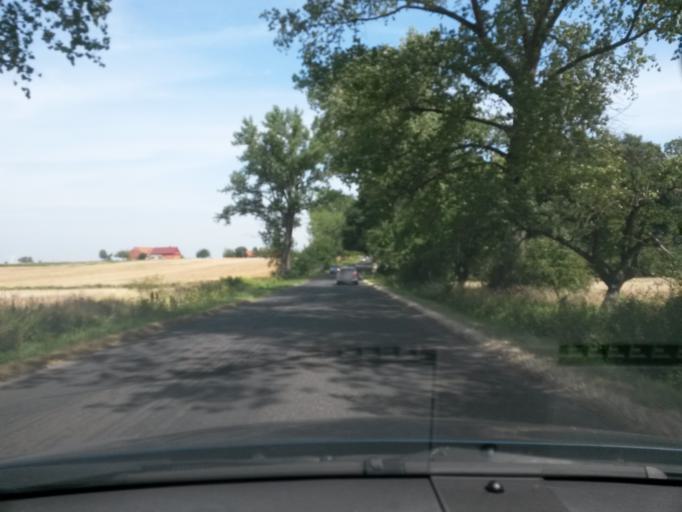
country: PL
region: Lower Silesian Voivodeship
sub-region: Powiat legnicki
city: Legnickie Pole
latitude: 51.1338
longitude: 16.3428
